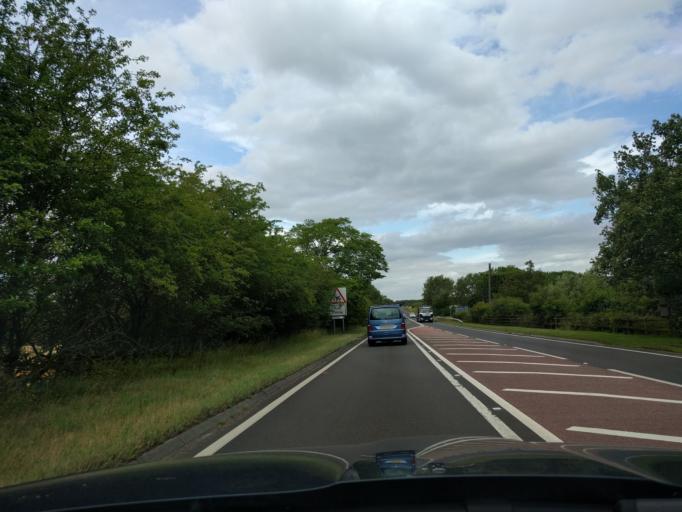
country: GB
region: England
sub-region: Northumberland
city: Felton
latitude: 55.2689
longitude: -1.7196
